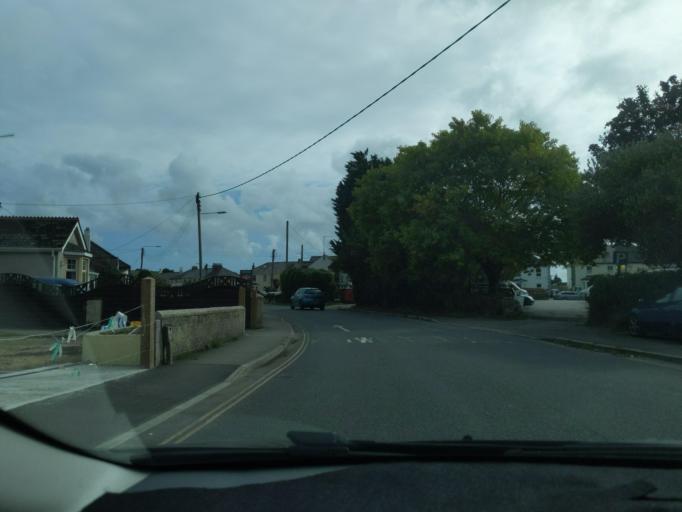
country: GB
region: England
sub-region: Cornwall
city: Par
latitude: 50.3524
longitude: -4.7002
